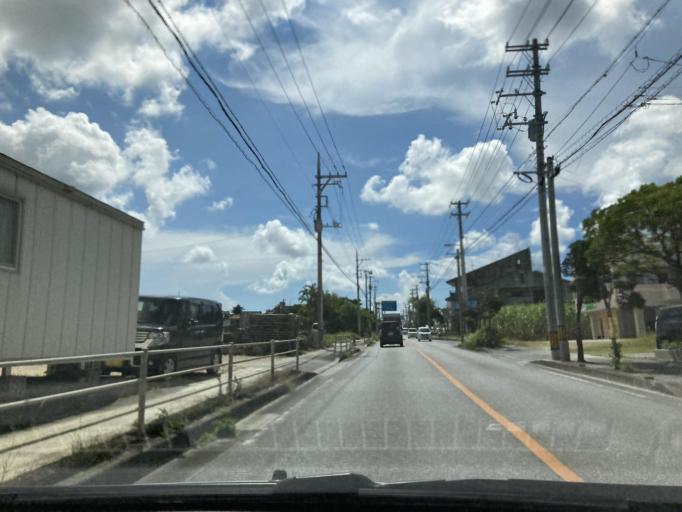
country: JP
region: Okinawa
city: Tomigusuku
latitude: 26.1493
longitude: 127.7242
